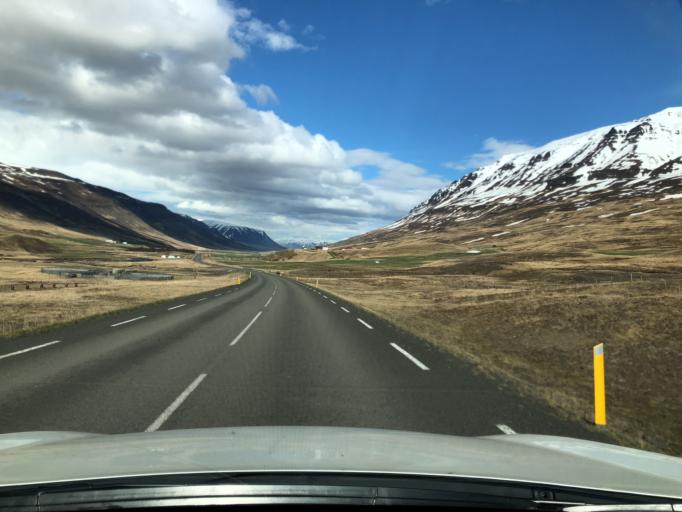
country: IS
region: Northeast
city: Dalvik
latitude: 65.5923
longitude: -18.5195
